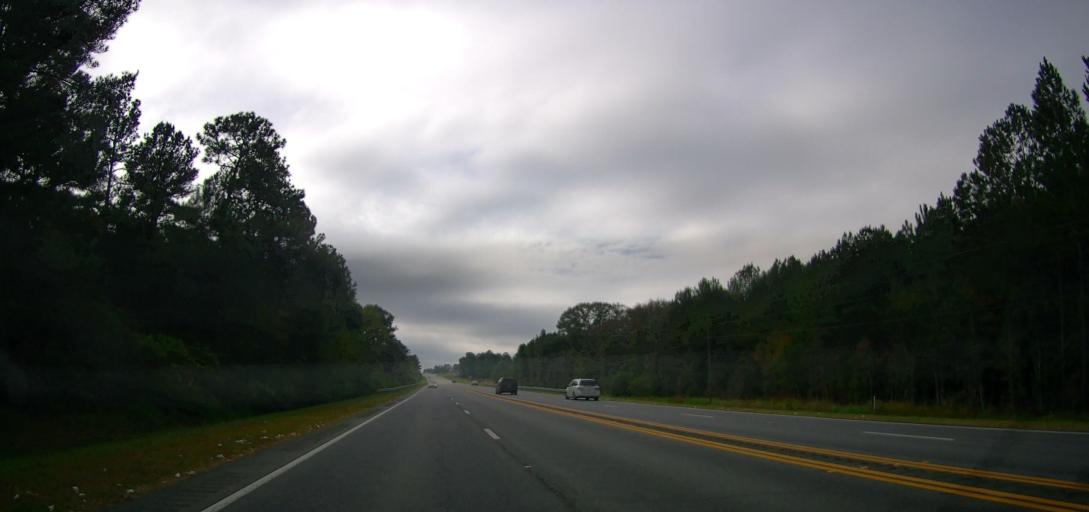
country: US
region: Georgia
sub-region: Tift County
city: Omega
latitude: 31.3831
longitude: -83.5535
